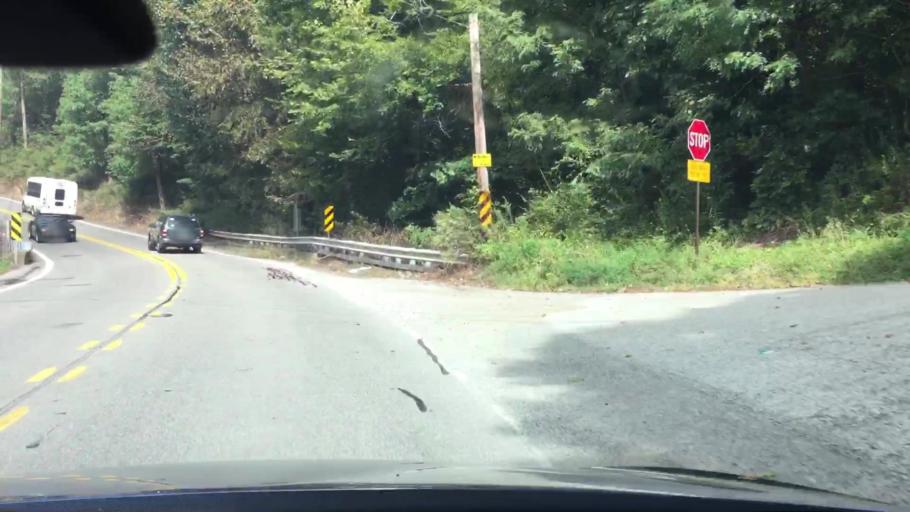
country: US
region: Pennsylvania
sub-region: Allegheny County
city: Cheswick
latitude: 40.5188
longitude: -79.8058
